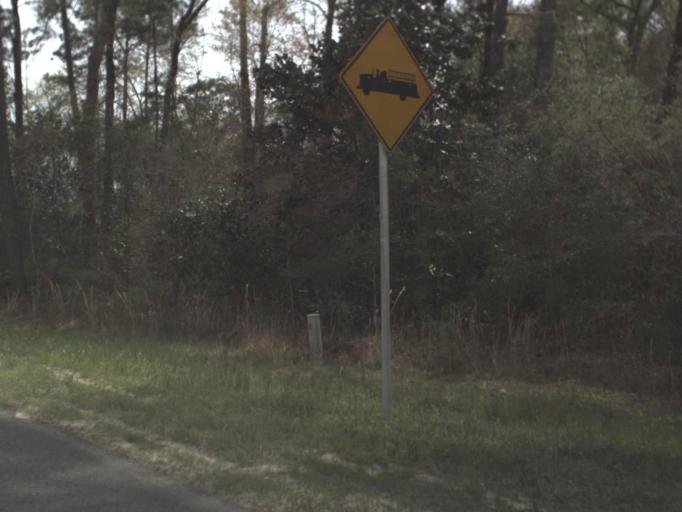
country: US
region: Alabama
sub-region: Geneva County
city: Geneva
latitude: 30.9528
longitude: -85.8806
